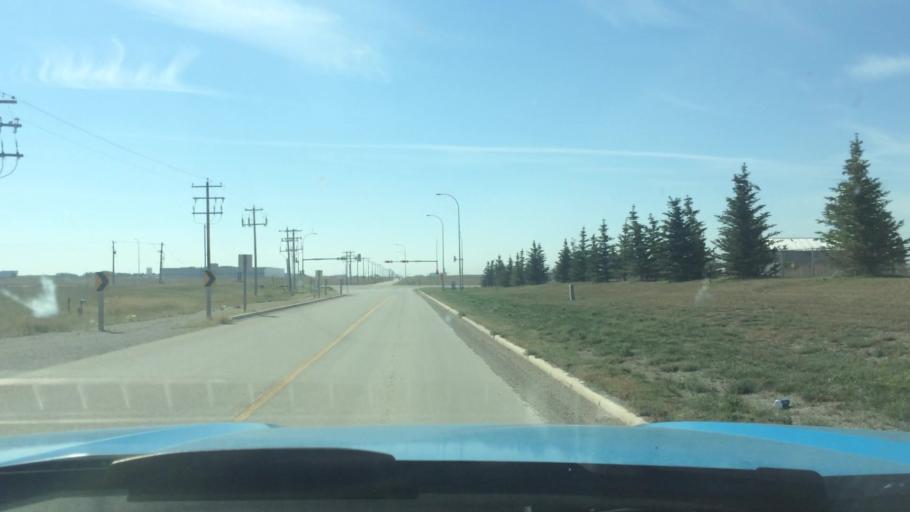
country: CA
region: Alberta
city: Airdrie
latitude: 51.2146
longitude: -113.9353
